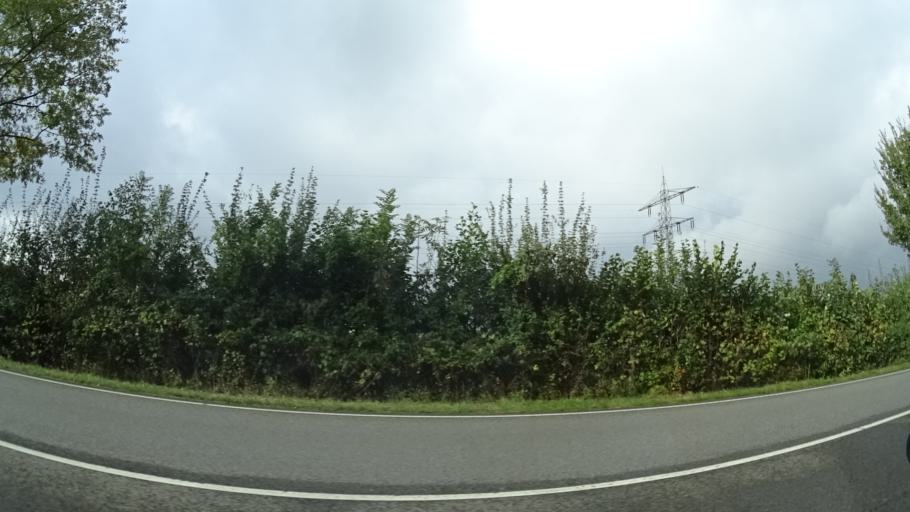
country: DE
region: Baden-Wuerttemberg
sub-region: Karlsruhe Region
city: Wiesloch
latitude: 49.2835
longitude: 8.6675
